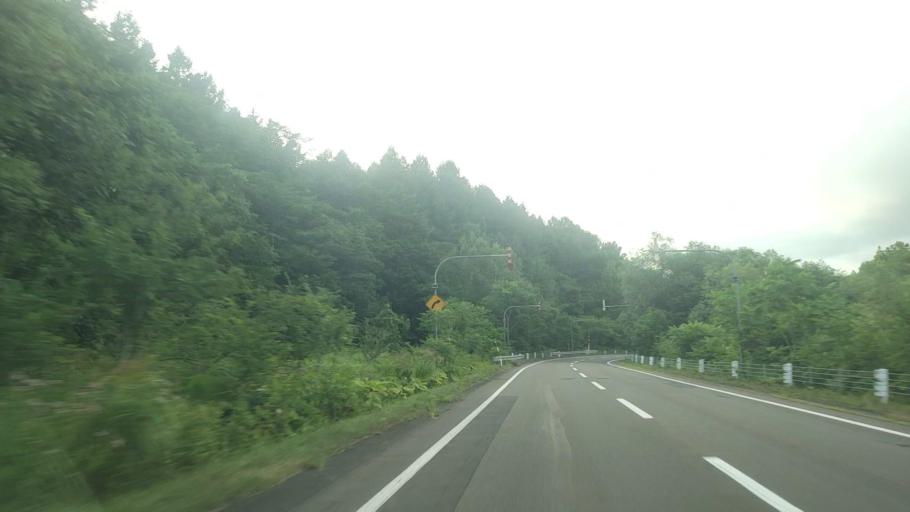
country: JP
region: Hokkaido
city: Bibai
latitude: 43.1250
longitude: 142.1020
